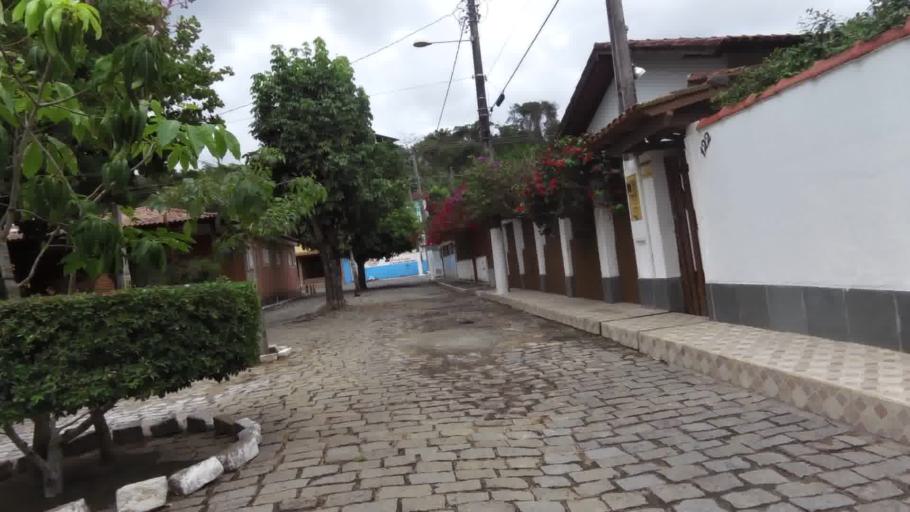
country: BR
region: Espirito Santo
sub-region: Marataizes
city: Marataizes
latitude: -21.0426
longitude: -40.8280
